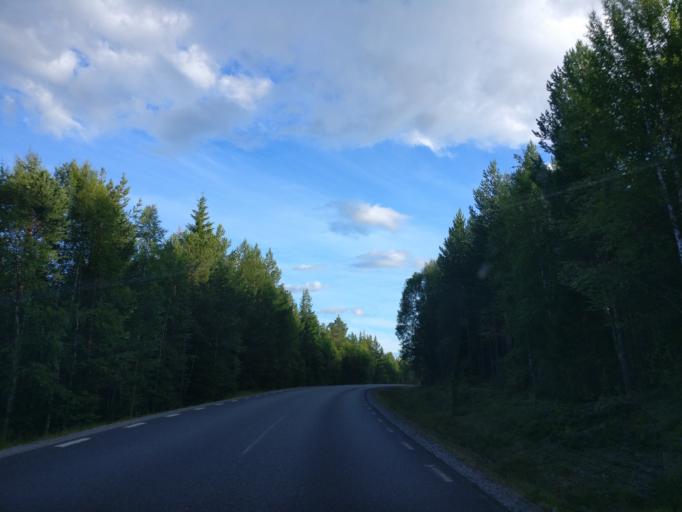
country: SE
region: Jaemtland
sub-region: Braecke Kommun
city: Braecke
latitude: 62.4432
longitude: 14.9871
